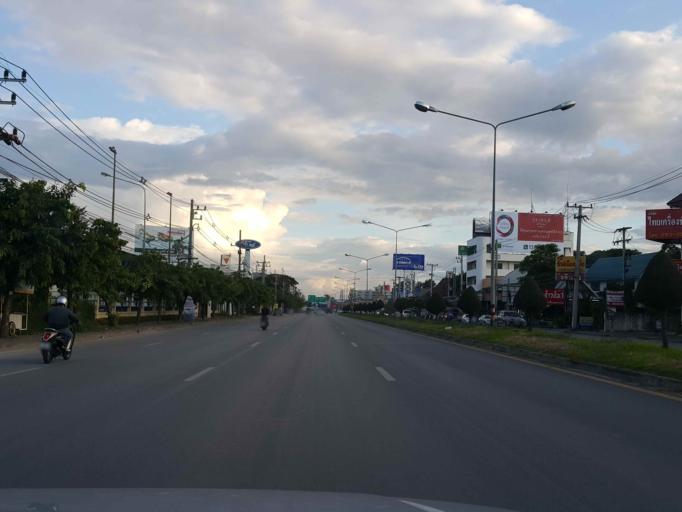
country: TH
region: Chiang Mai
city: Chiang Mai
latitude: 18.8158
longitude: 99.0114
